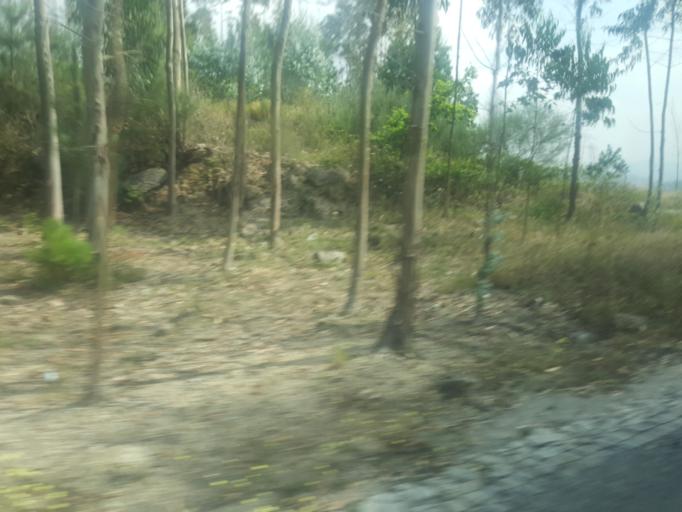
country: PT
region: Porto
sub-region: Marco de Canaveses
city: Marco de Canavezes
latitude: 41.1701
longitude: -8.1940
